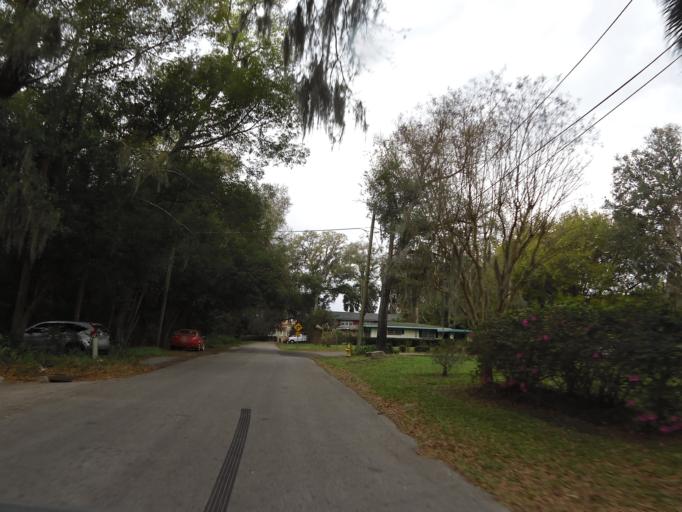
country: US
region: Florida
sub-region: Duval County
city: Jacksonville
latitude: 30.3419
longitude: -81.6073
